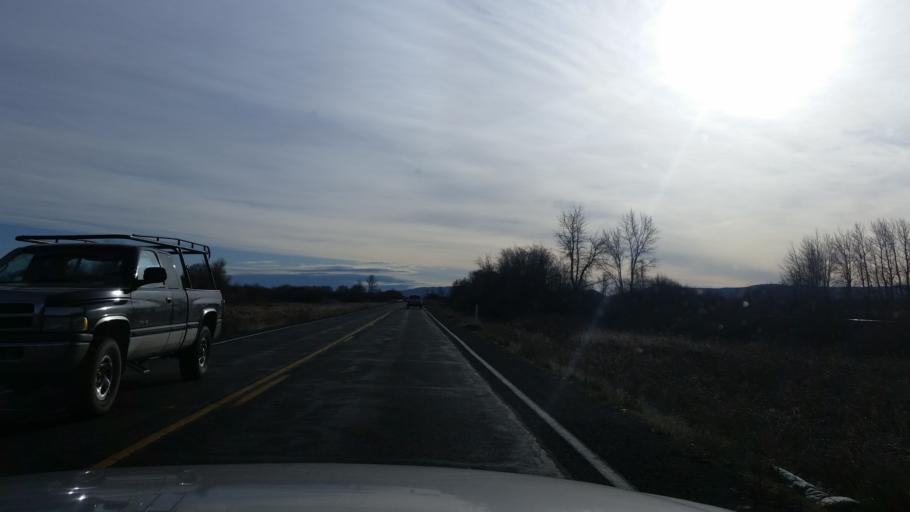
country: US
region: Washington
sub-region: Kittitas County
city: Ellensburg
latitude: 47.0405
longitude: -120.6196
